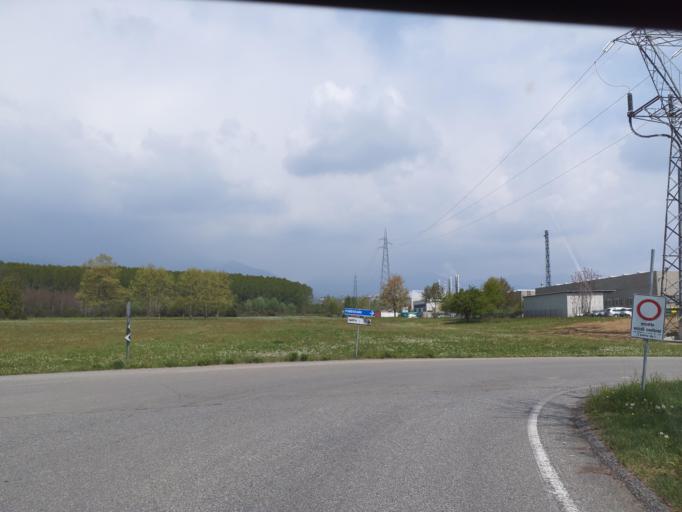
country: IT
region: Piedmont
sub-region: Provincia di Biella
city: Ponderano
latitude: 45.5436
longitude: 8.0473
